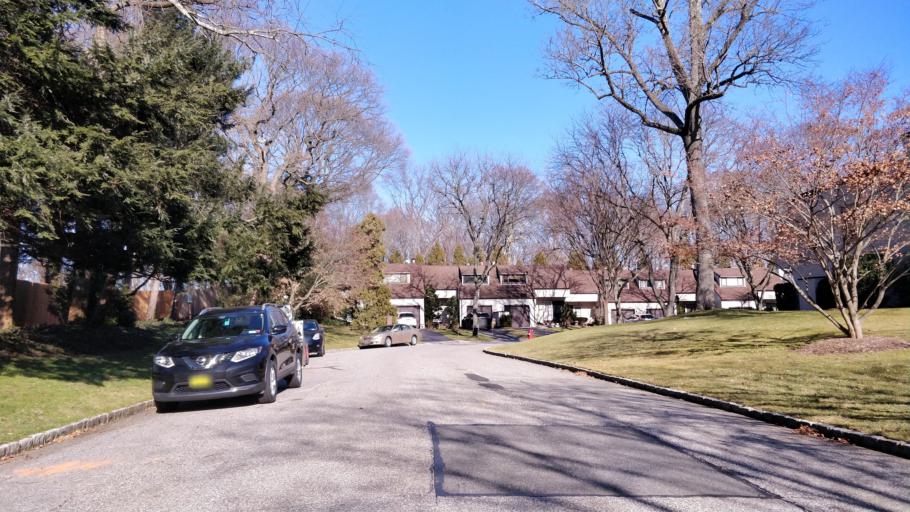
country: US
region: New York
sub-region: Nassau County
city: Glen Head
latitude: 40.8402
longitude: -73.6262
